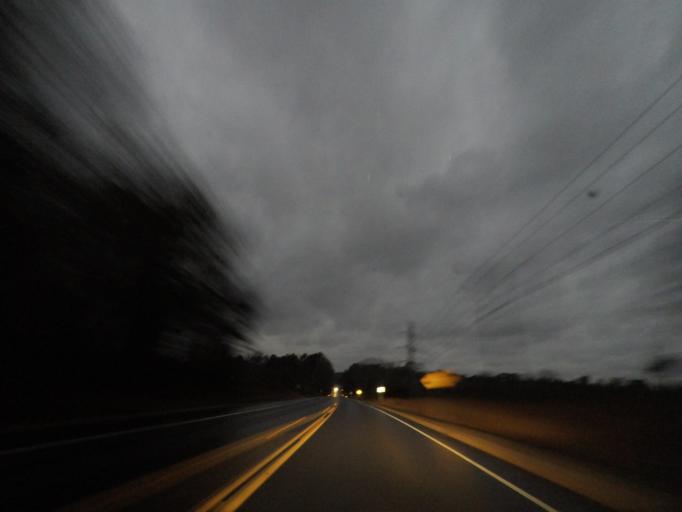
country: US
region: North Carolina
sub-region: Orange County
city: Hillsborough
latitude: 36.0432
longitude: -79.0170
